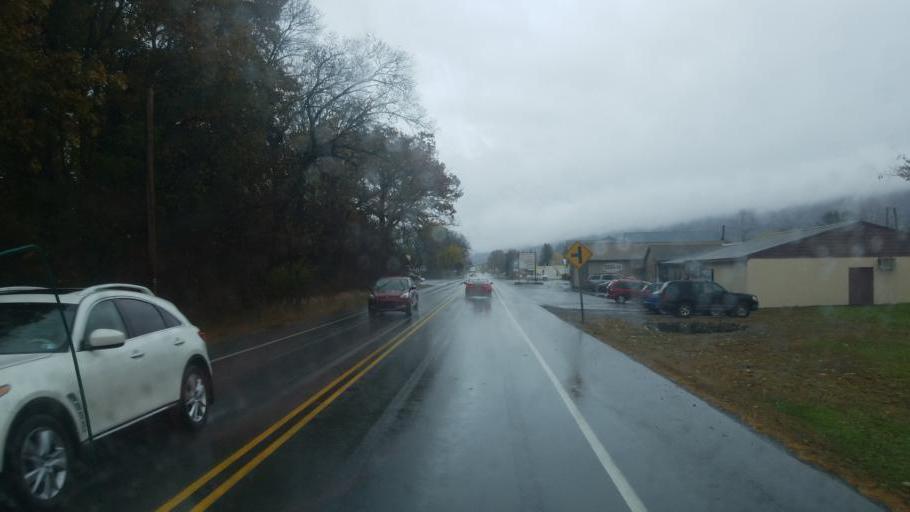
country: US
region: Pennsylvania
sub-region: Clinton County
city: Mill Hall
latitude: 41.1126
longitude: -77.4937
